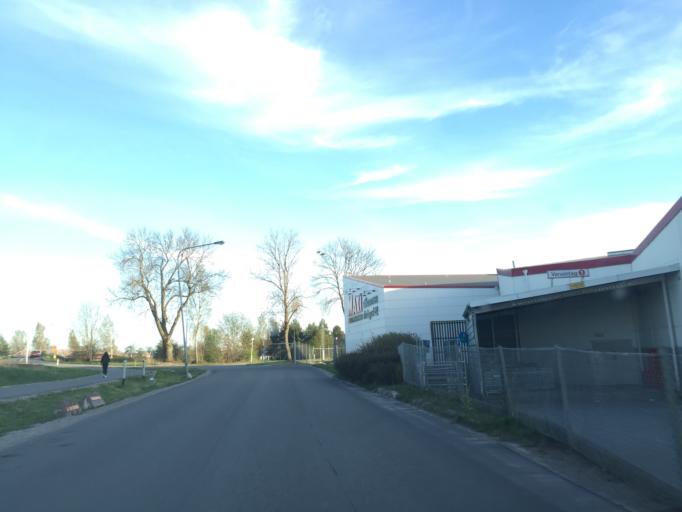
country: SE
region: OErebro
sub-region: Orebro Kommun
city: Orebro
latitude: 59.2963
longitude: 15.2072
